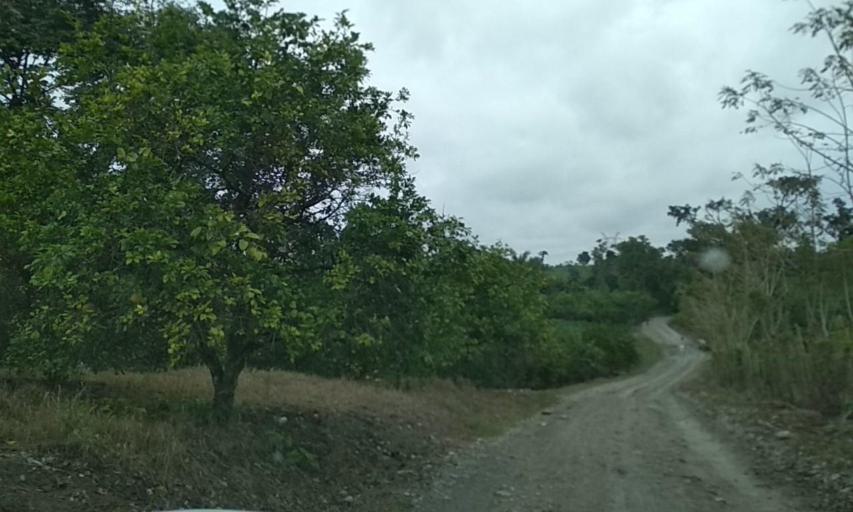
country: MX
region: Puebla
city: Espinal
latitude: 20.3057
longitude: -97.4161
